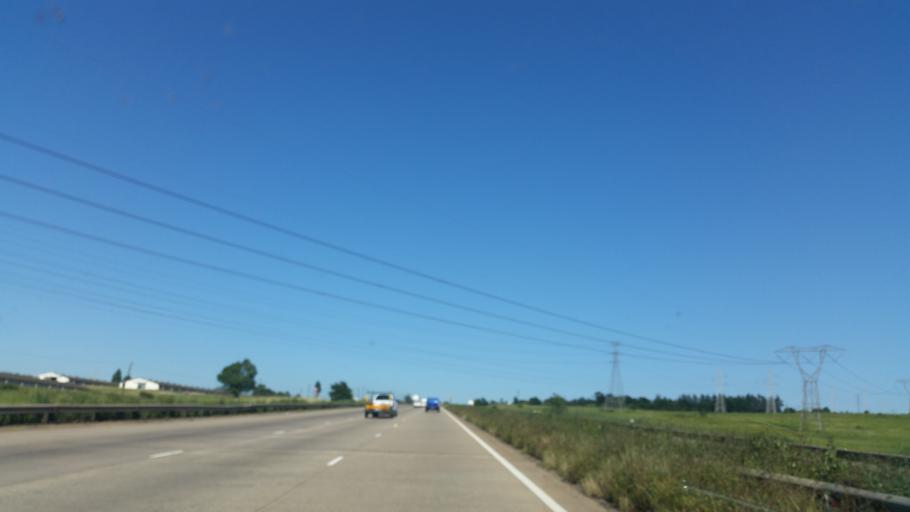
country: ZA
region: KwaZulu-Natal
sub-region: eThekwini Metropolitan Municipality
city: Mpumalanga
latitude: -29.7389
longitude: 30.6188
